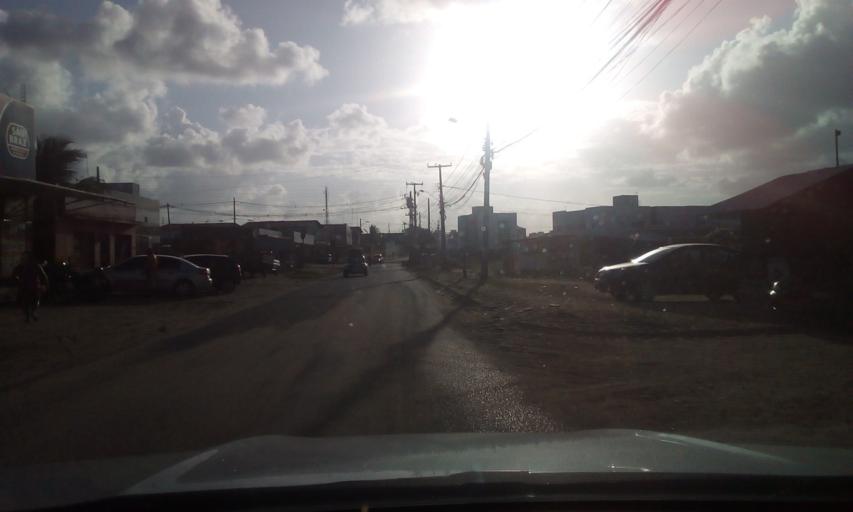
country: BR
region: Paraiba
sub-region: Conde
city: Conde
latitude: -7.2083
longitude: -34.8354
